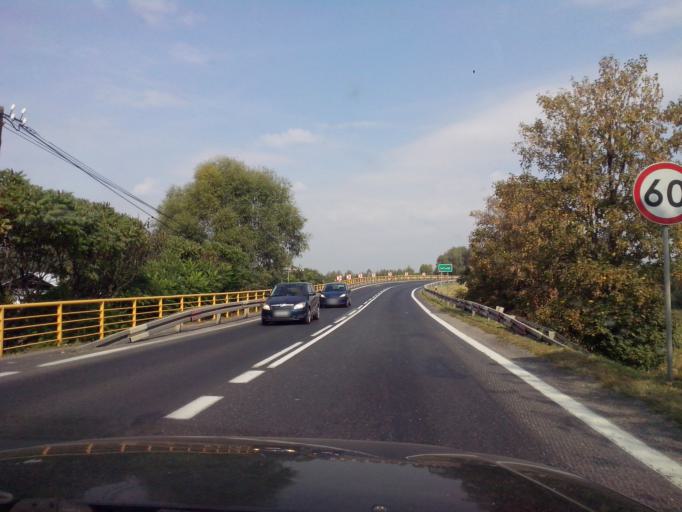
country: PL
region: Subcarpathian Voivodeship
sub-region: Powiat rzeszowski
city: Lutoryz
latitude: 49.9708
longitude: 21.9215
